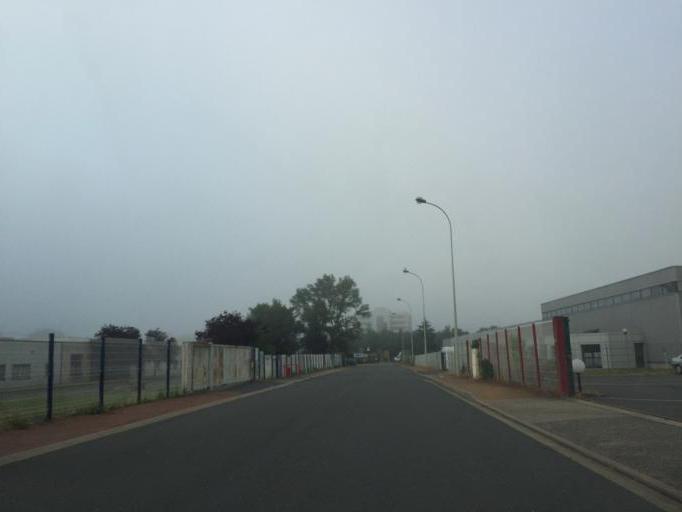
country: FR
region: Rhone-Alpes
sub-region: Departement de l'Ain
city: Jassans-Riottier
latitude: 45.9864
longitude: 4.7457
